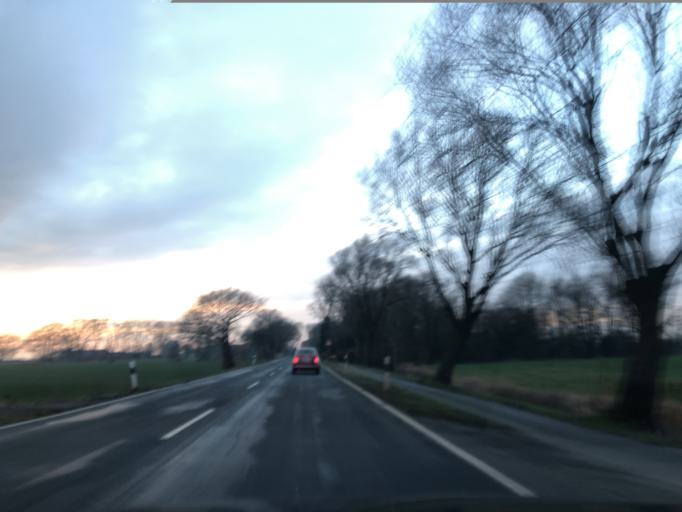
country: DE
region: Lower Saxony
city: Lemwerder
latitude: 53.1351
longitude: 8.6097
